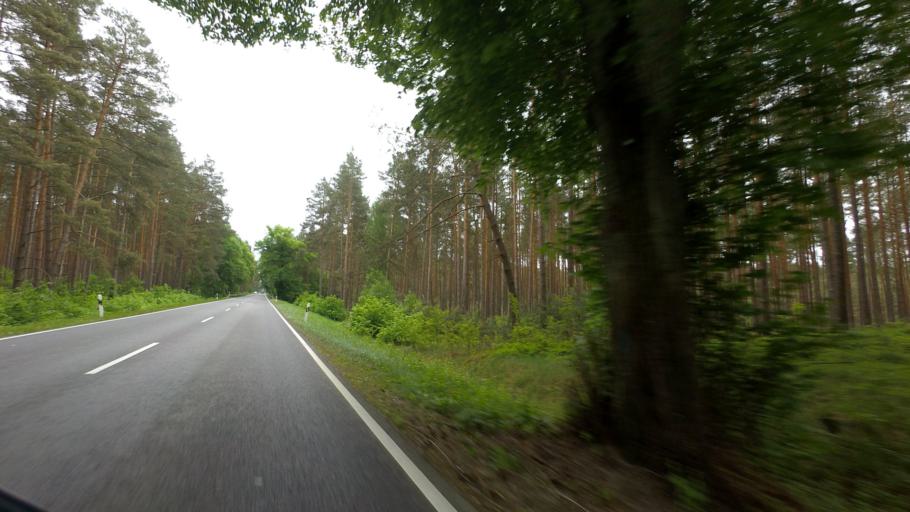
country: DE
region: Brandenburg
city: Furstenberg
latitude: 53.2342
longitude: 13.1151
